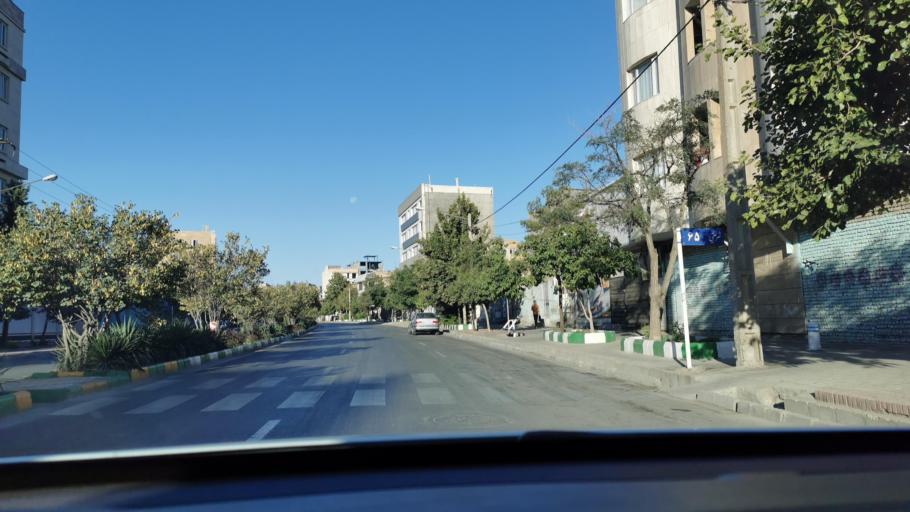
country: IR
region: Razavi Khorasan
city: Mashhad
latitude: 36.3509
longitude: 59.4802
